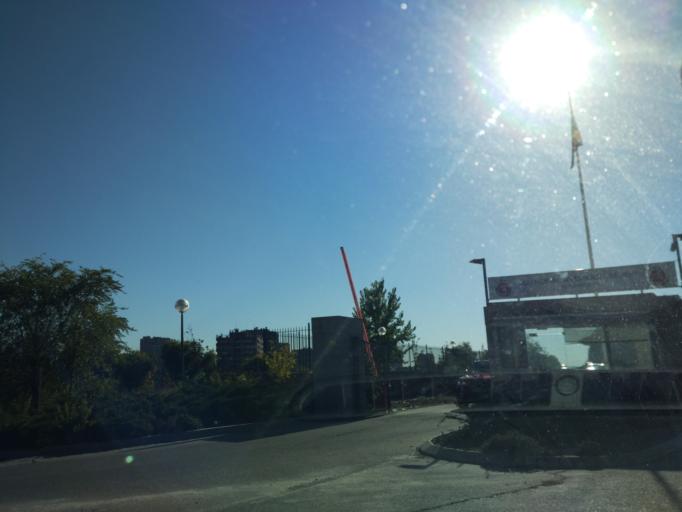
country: ES
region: Madrid
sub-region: Provincia de Madrid
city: Fuencarral-El Pardo
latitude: 40.4864
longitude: -3.7356
